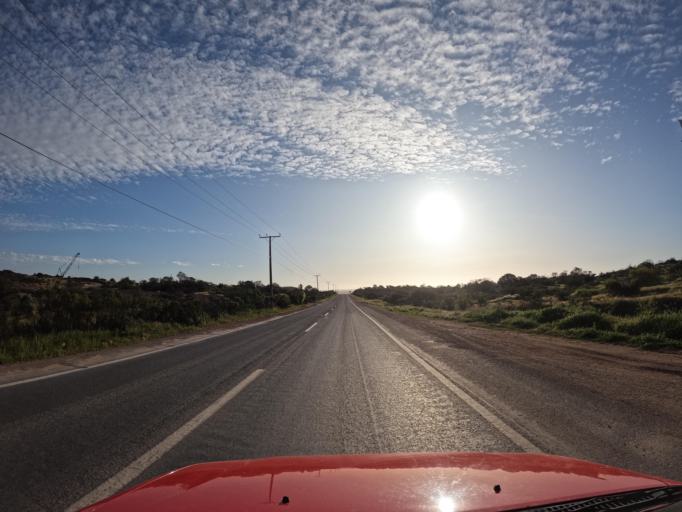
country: CL
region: Valparaiso
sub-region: San Antonio Province
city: San Antonio
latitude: -34.0863
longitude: -71.6723
